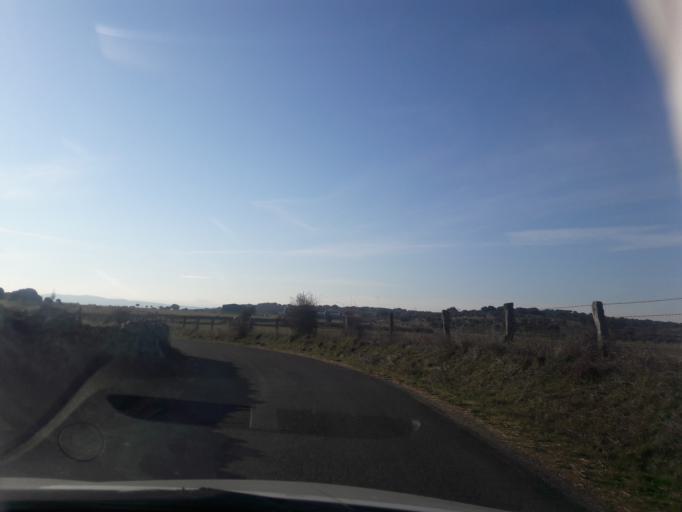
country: ES
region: Castille and Leon
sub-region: Provincia de Salamanca
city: Montejo
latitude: 40.6290
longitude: -5.6202
